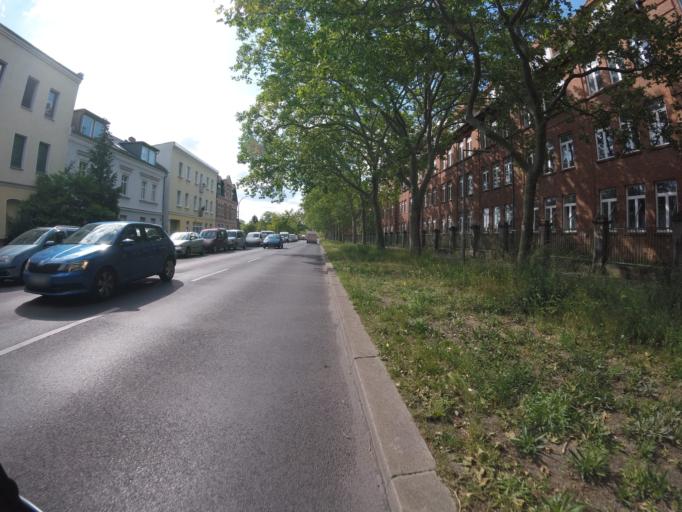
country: DE
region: Berlin
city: Wilhelmstadt
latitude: 52.5230
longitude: 13.1863
